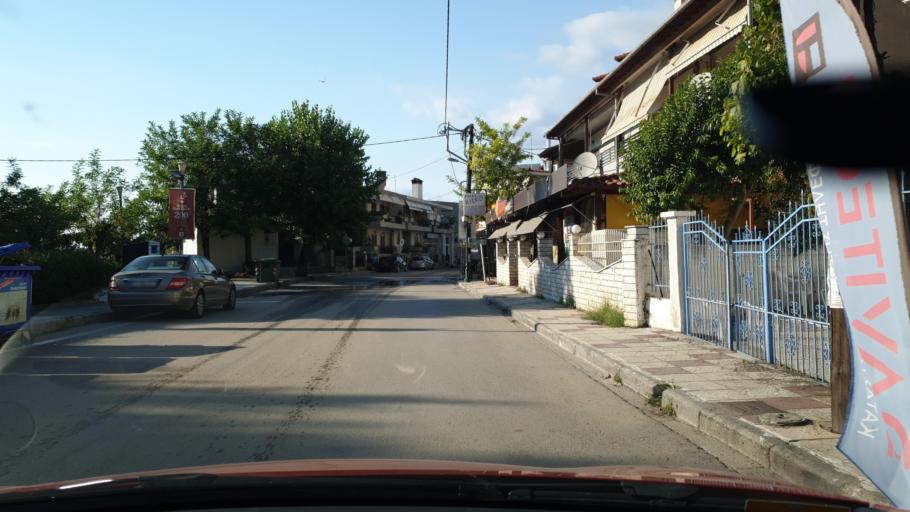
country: GR
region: Central Macedonia
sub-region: Nomos Thessalonikis
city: Vasilika
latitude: 40.4809
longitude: 23.1368
